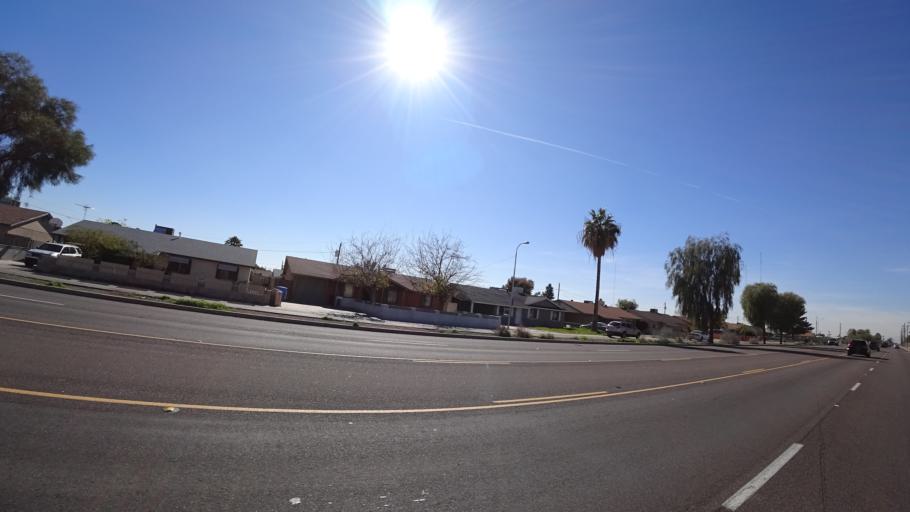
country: US
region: Arizona
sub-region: Maricopa County
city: Glendale
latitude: 33.5092
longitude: -112.2145
